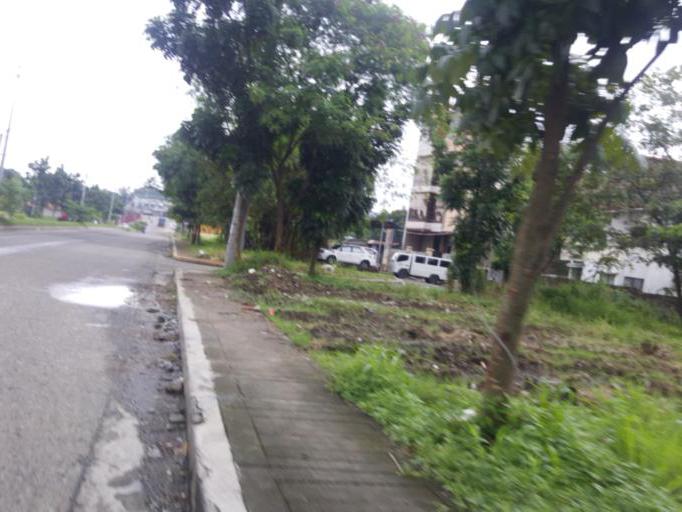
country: PH
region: Calabarzon
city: Bagong Pagasa
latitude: 14.7164
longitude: 121.0208
